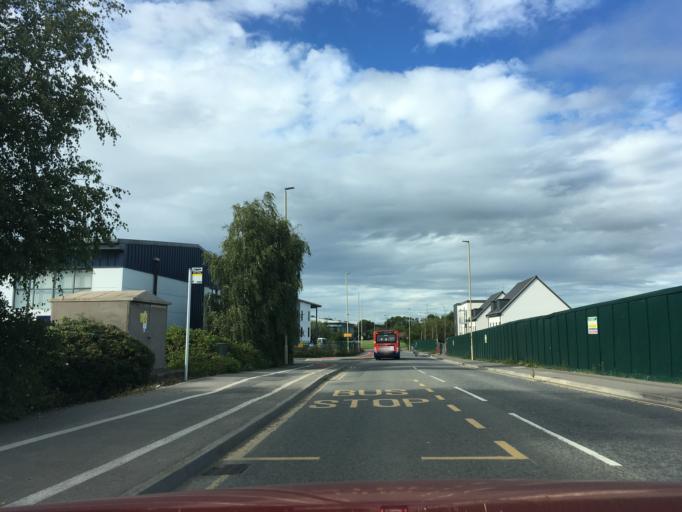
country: GB
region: England
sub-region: Gloucestershire
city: Gloucester
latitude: 51.8104
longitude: -2.2689
